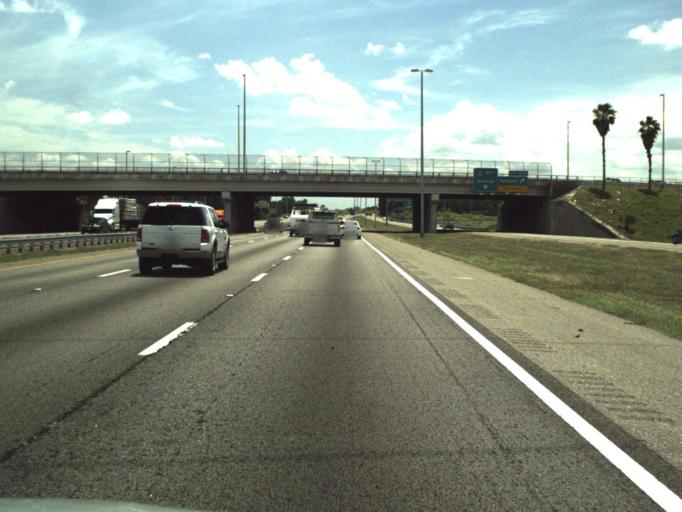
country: US
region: Florida
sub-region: Volusia County
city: Deltona
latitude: 28.9125
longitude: -81.2715
